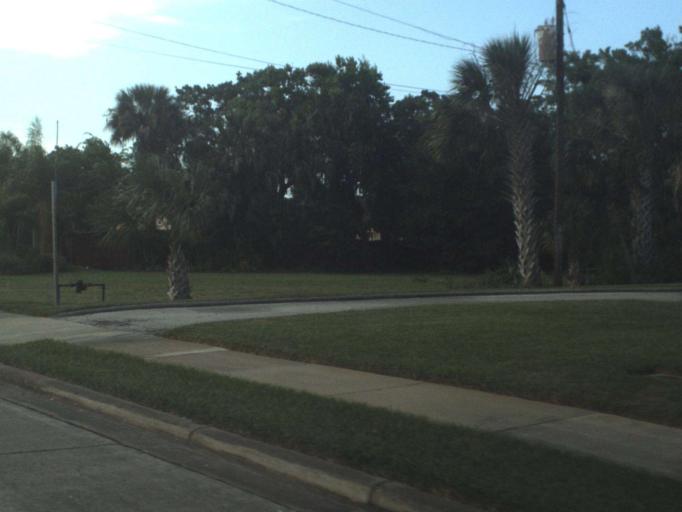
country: US
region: Florida
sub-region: Volusia County
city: Port Orange
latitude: 29.1473
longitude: -80.9894
